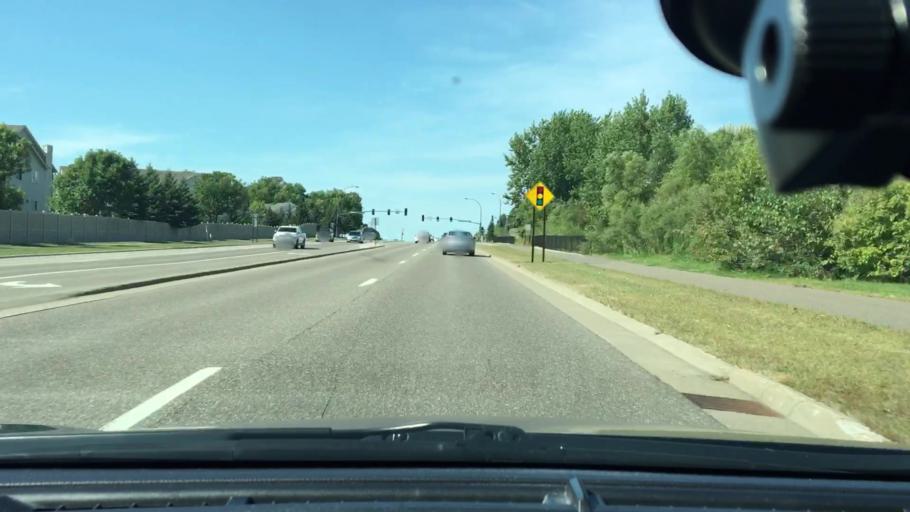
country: US
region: Minnesota
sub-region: Hennepin County
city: Maple Grove
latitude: 45.0842
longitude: -93.4842
